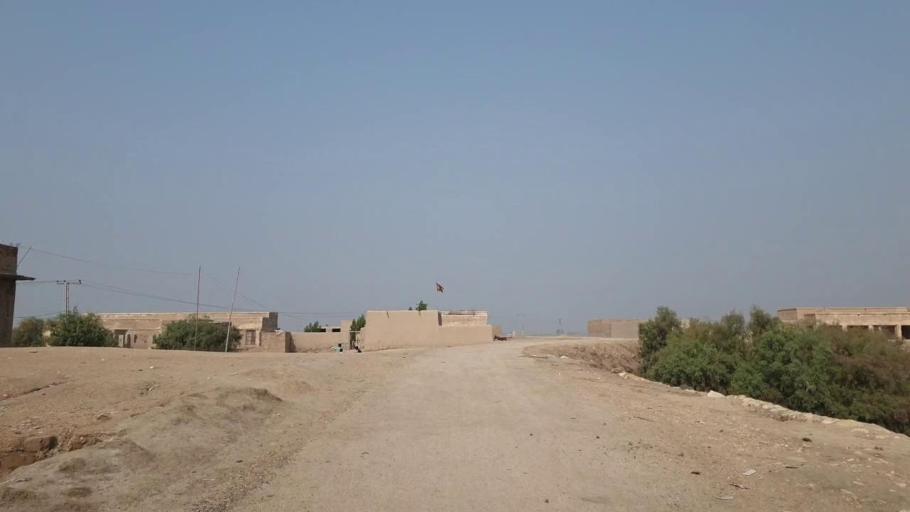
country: PK
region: Sindh
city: Bhan
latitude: 26.4465
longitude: 67.7143
